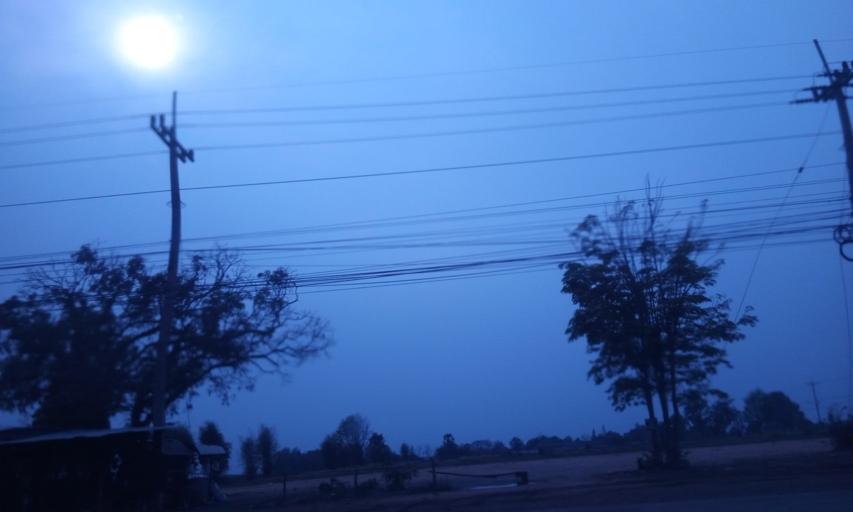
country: TH
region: Chachoengsao
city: Plaeng Yao
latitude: 13.5481
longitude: 101.2634
